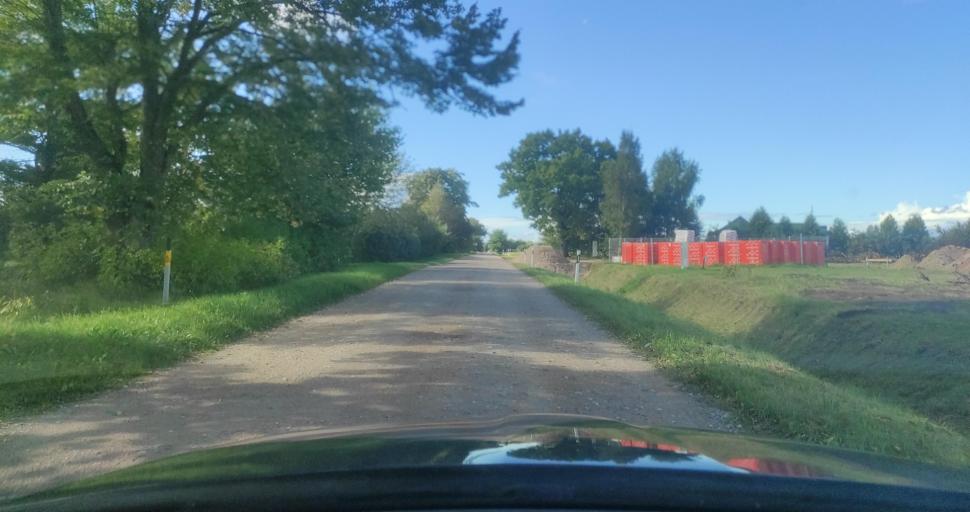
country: LV
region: Ventspils
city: Ventspils
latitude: 57.3655
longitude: 21.6116
